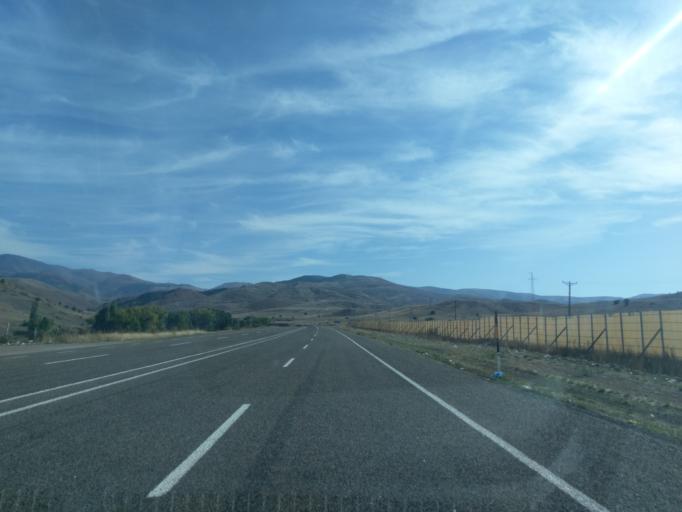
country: TR
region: Sivas
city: Imranli
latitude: 39.8371
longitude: 38.2760
